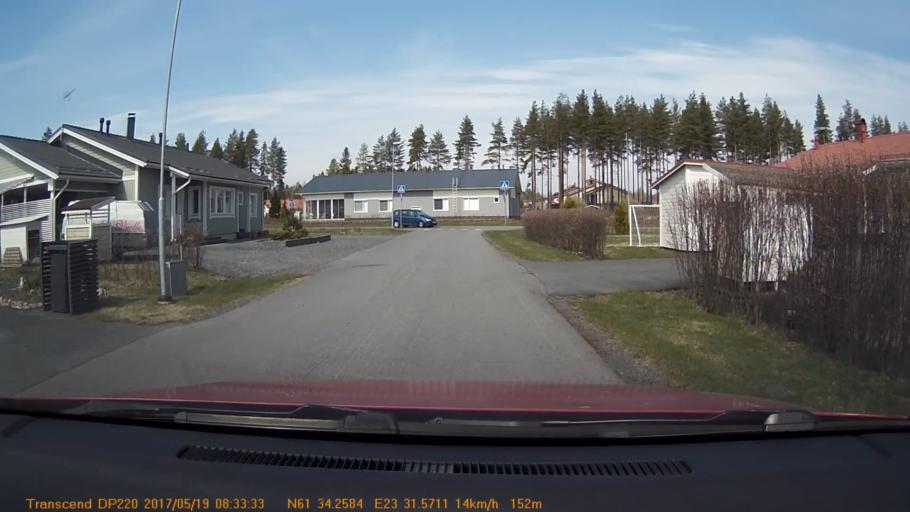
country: FI
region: Pirkanmaa
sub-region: Tampere
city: Yloejaervi
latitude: 61.5710
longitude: 23.5261
